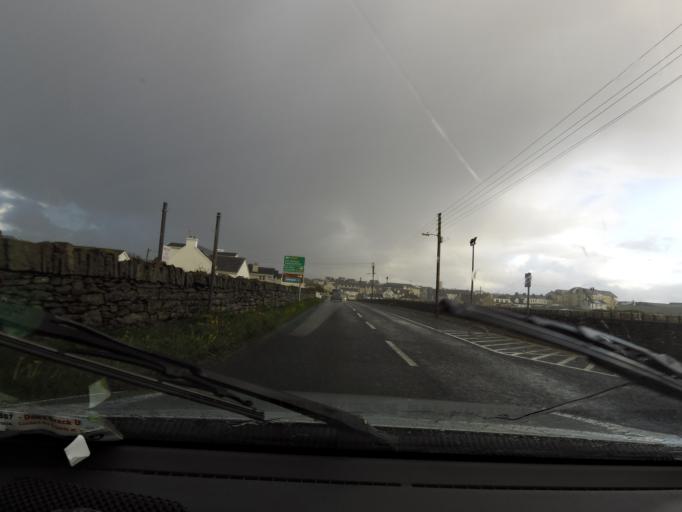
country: IE
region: Munster
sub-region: An Clar
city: Kilrush
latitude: 52.9355
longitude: -9.3451
